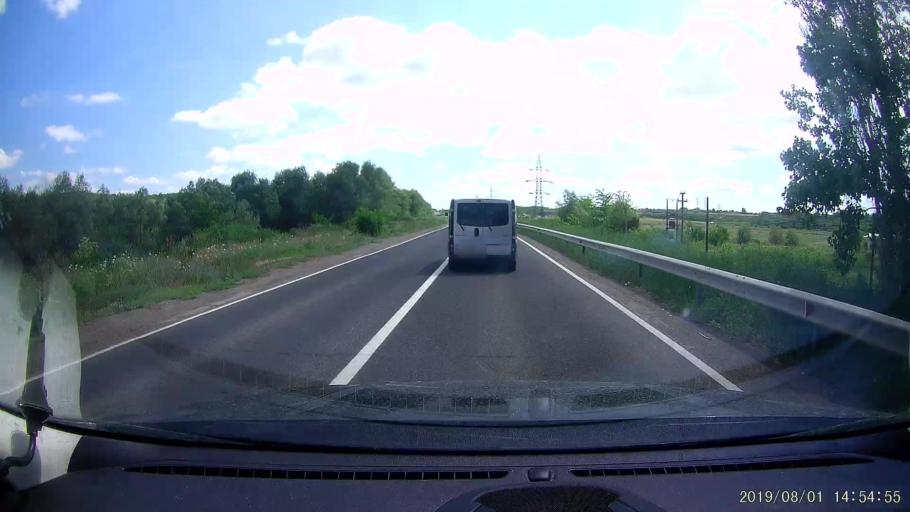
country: RO
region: Braila
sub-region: Municipiul Braila
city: Braila
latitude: 45.3115
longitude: 27.9832
